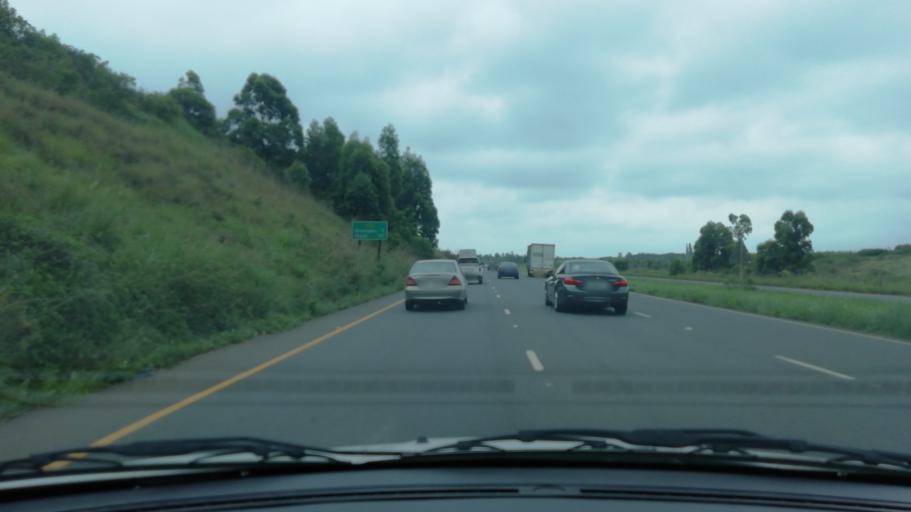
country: ZA
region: KwaZulu-Natal
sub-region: uThungulu District Municipality
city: Empangeni
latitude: -28.7683
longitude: 31.9277
